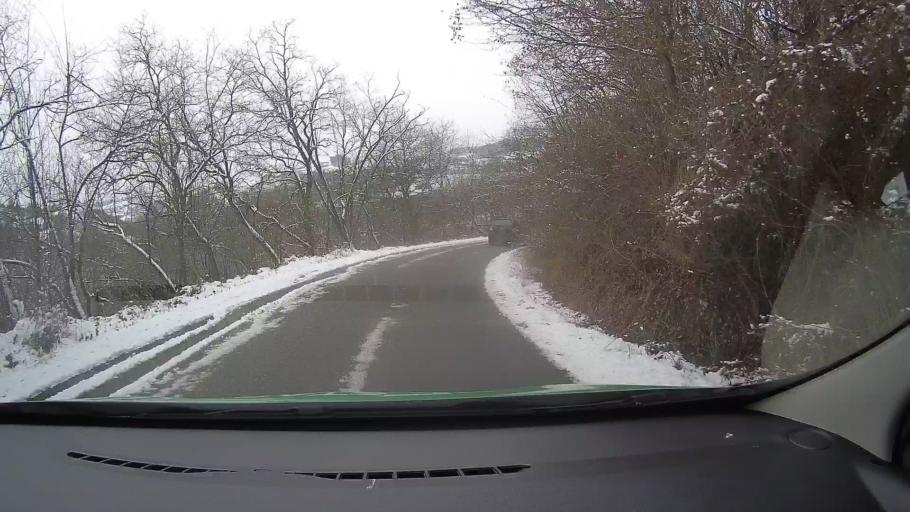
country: RO
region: Alba
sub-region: Comuna Almasu Mare
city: Almasu Mare
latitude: 46.0813
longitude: 23.1223
